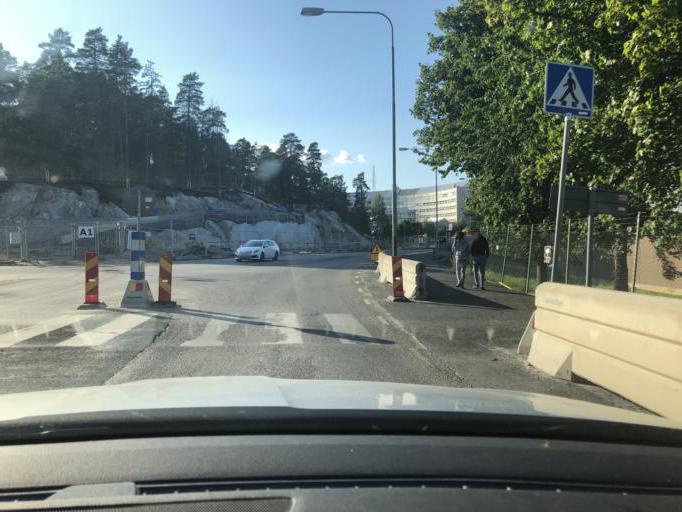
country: SE
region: Stockholm
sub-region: Stockholms Kommun
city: Kista
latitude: 59.3791
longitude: 17.9410
